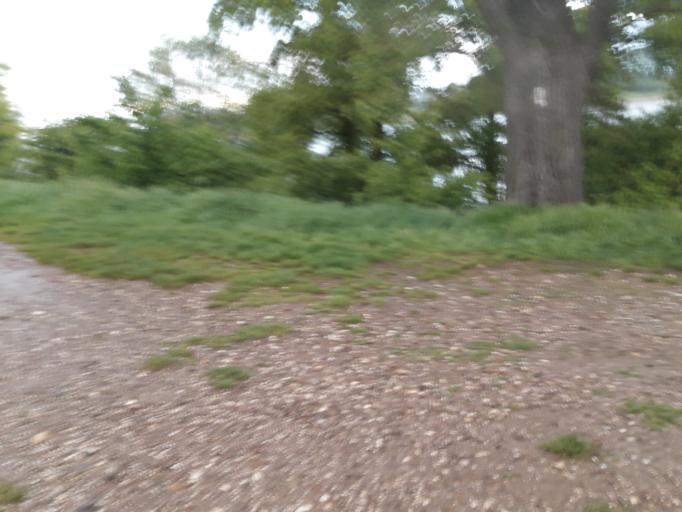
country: DE
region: North Rhine-Westphalia
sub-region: Regierungsbezirk Dusseldorf
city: Meerbusch
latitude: 51.2721
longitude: 6.6990
